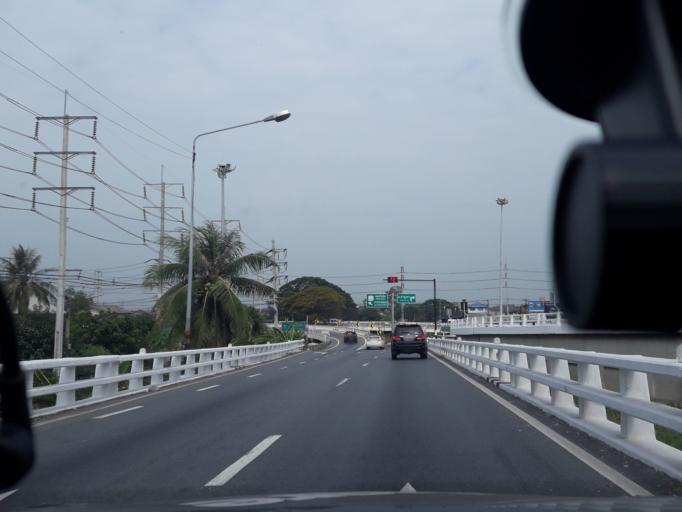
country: TH
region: Pathum Thani
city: Lam Luk Ka
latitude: 13.9320
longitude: 100.7067
